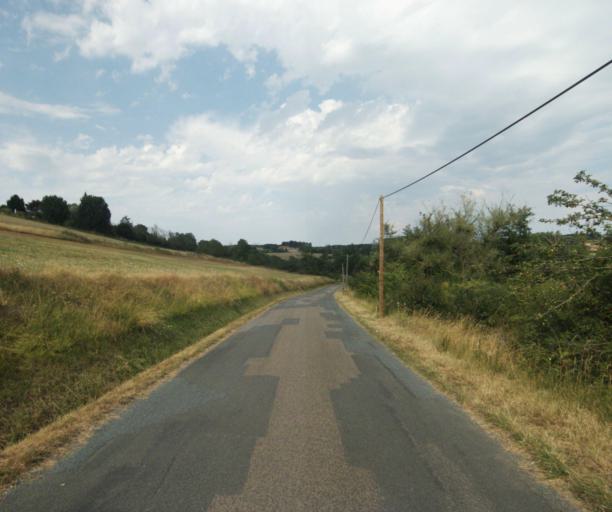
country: FR
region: Rhone-Alpes
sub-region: Departement du Rhone
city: Bully
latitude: 45.8558
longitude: 4.5911
